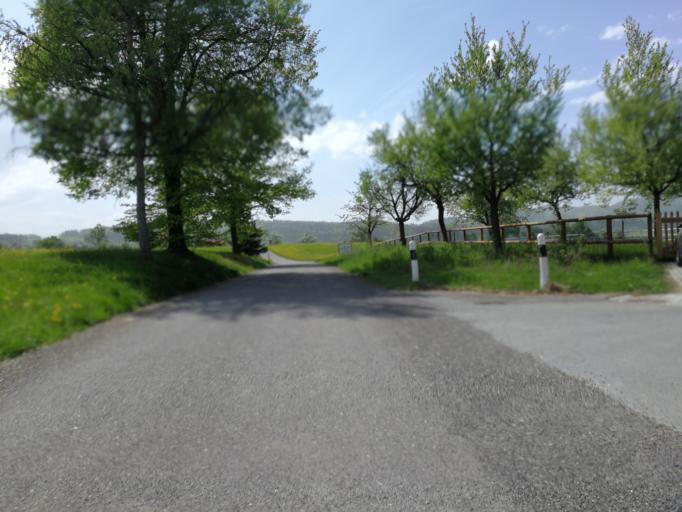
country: CH
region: Zurich
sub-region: Bezirk Meilen
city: Oetwil am See
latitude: 47.2791
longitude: 8.7375
